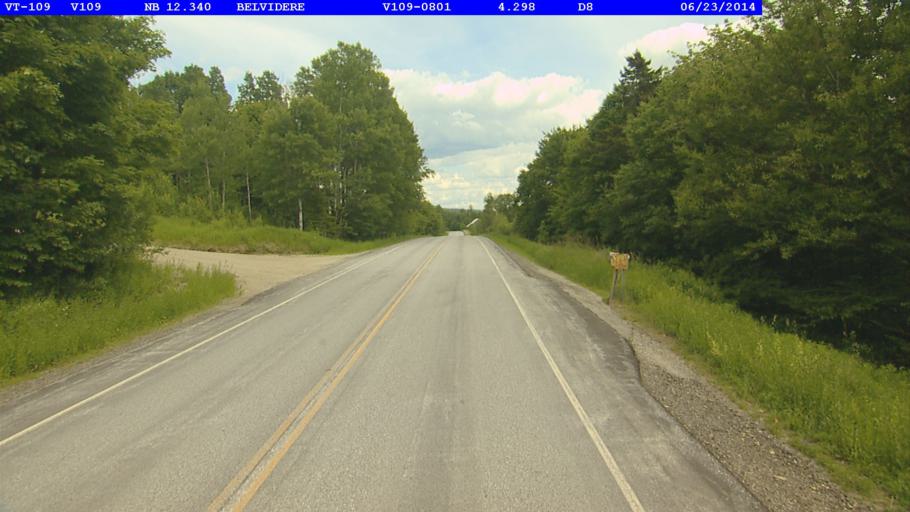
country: US
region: Vermont
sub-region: Lamoille County
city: Johnson
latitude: 44.7597
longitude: -72.6707
